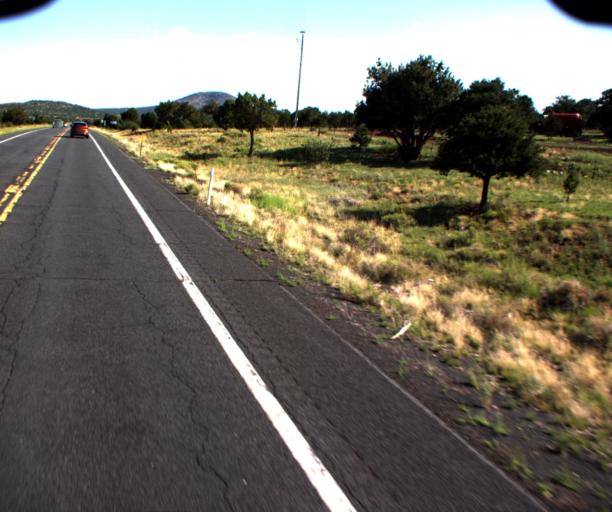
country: US
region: Arizona
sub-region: Coconino County
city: Williams
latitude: 35.3476
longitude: -112.1667
